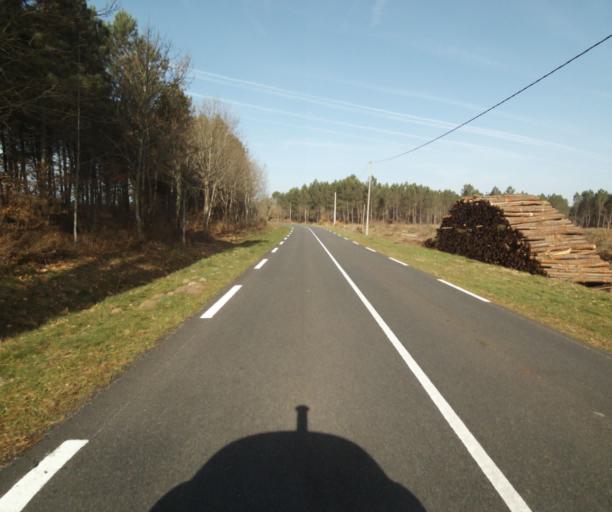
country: FR
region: Aquitaine
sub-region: Departement de la Gironde
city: Grignols
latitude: 44.2074
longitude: -0.1554
